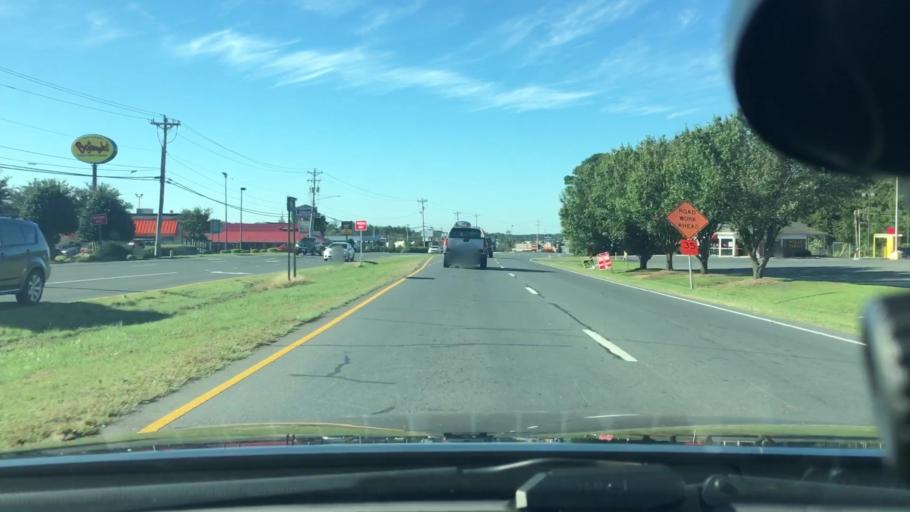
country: US
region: North Carolina
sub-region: Stanly County
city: Albemarle
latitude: 35.3473
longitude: -80.1676
